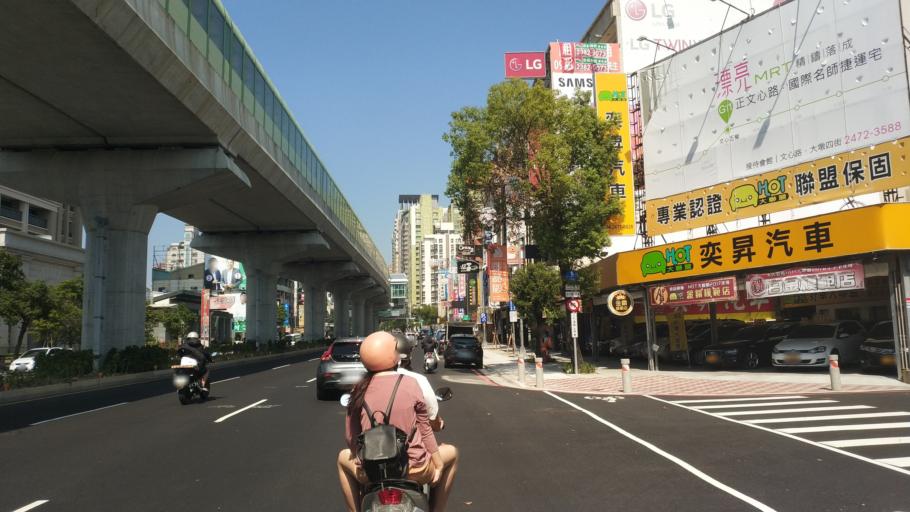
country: TW
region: Taiwan
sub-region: Taichung City
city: Taichung
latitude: 24.1379
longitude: 120.6467
